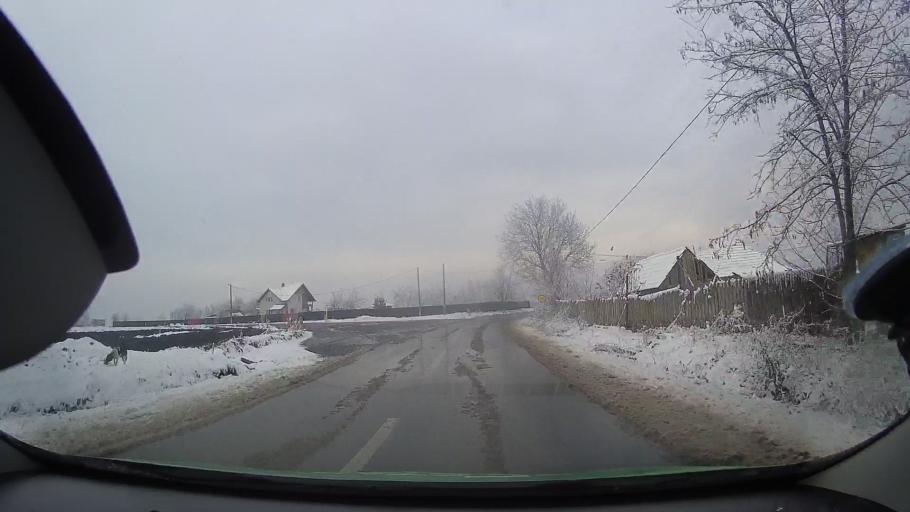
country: RO
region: Mures
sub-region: Comuna Bogata
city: Bogata
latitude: 46.4535
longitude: 24.0822
